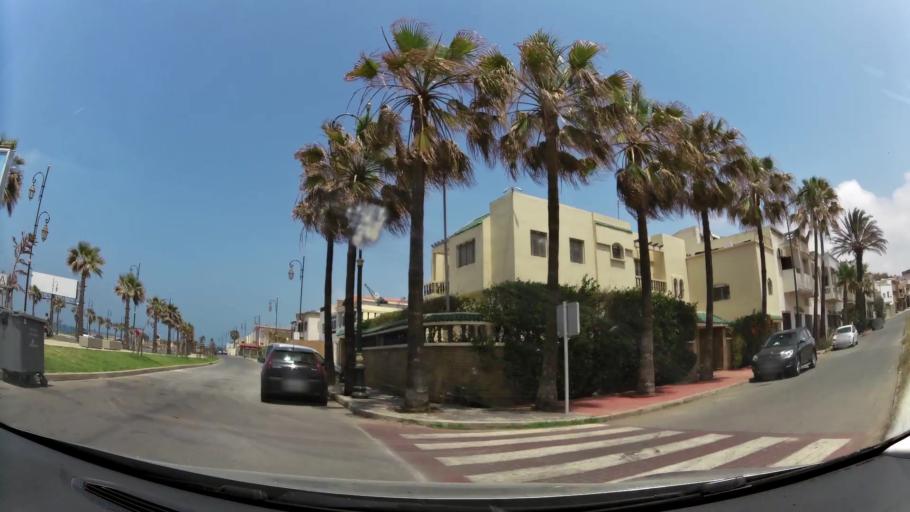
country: MA
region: Rabat-Sale-Zemmour-Zaer
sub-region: Skhirate-Temara
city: Temara
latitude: 33.9774
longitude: -6.8969
